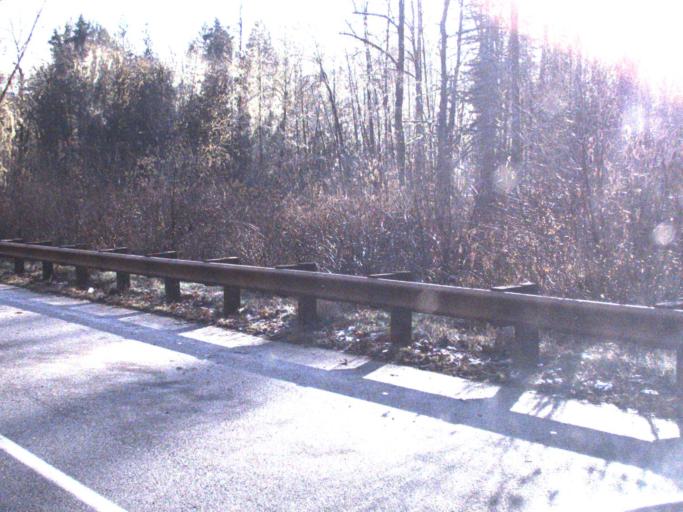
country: US
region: Washington
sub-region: Snohomish County
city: Darrington
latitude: 48.3776
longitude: -121.5512
